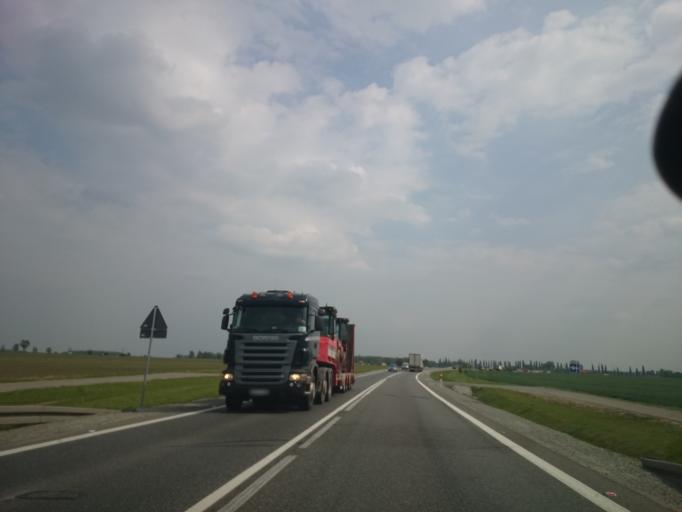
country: PL
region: Lower Silesian Voivodeship
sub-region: Powiat wroclawski
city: Kobierzyce
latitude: 50.9977
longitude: 16.9482
